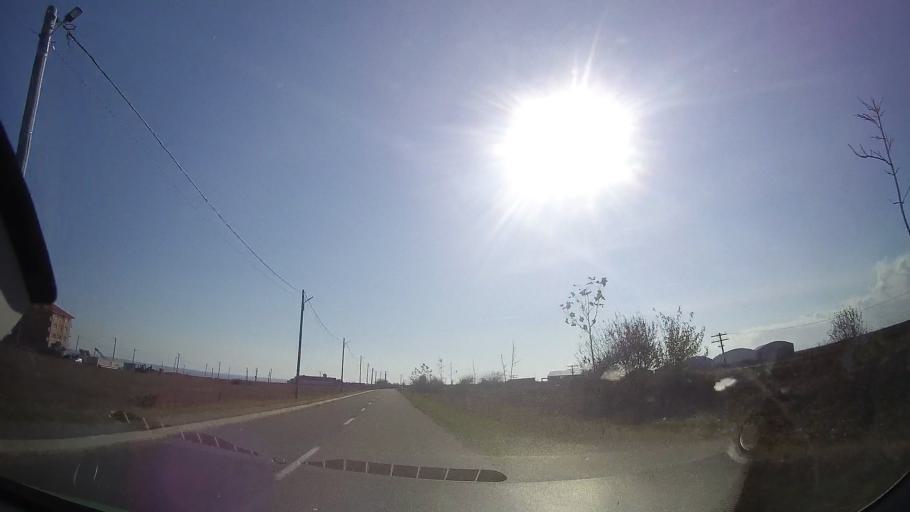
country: RO
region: Constanta
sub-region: Comuna Costinesti
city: Schitu
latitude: 43.9280
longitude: 28.6322
